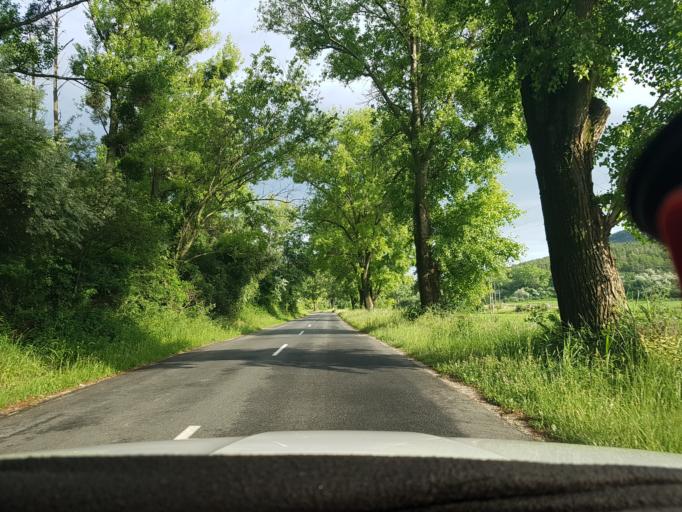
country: HU
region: Komarom-Esztergom
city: Labatlan
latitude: 47.7322
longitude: 18.5285
